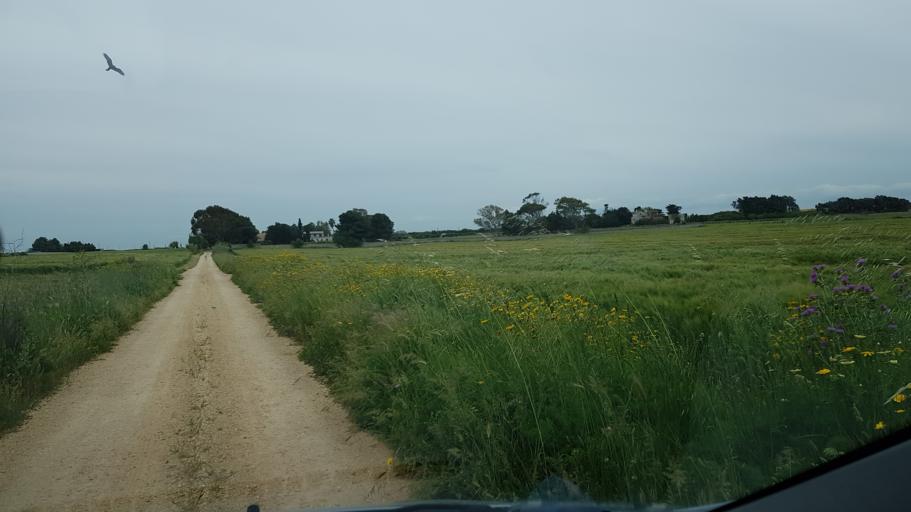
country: IT
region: Apulia
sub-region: Provincia di Brindisi
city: Brindisi
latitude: 40.6520
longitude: 17.8824
